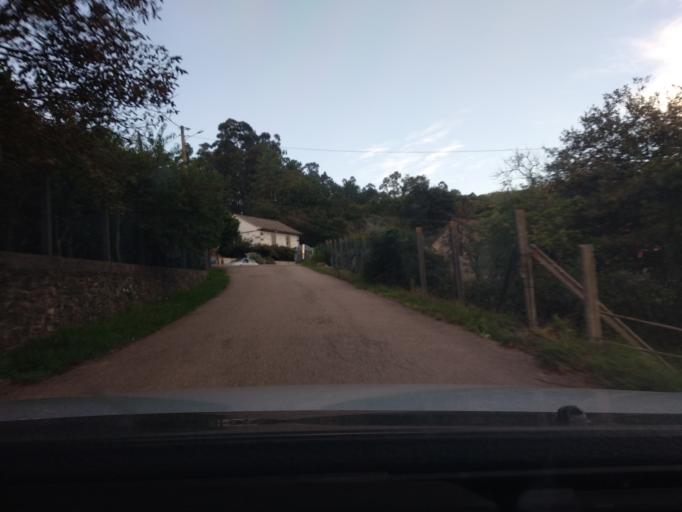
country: ES
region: Galicia
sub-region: Provincia de Pontevedra
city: Moana
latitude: 42.3059
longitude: -8.6987
